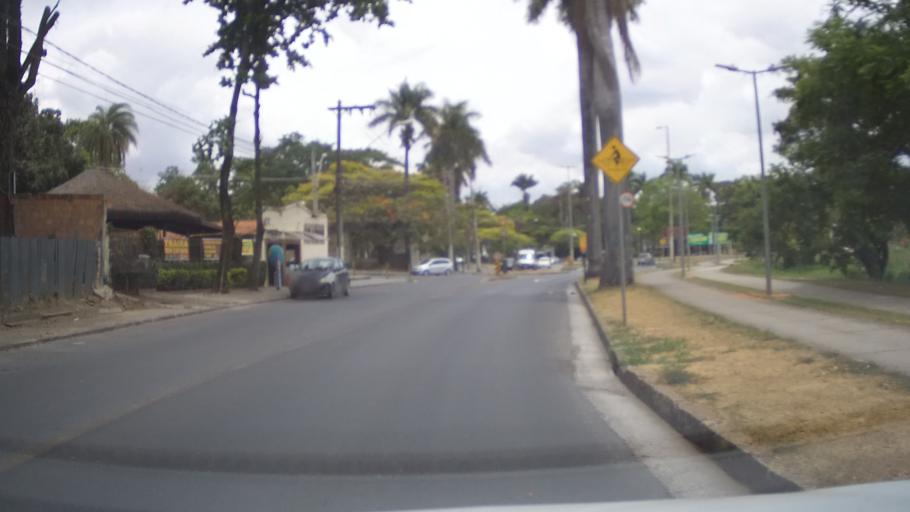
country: BR
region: Minas Gerais
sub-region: Contagem
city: Contagem
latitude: -19.8541
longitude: -44.0038
